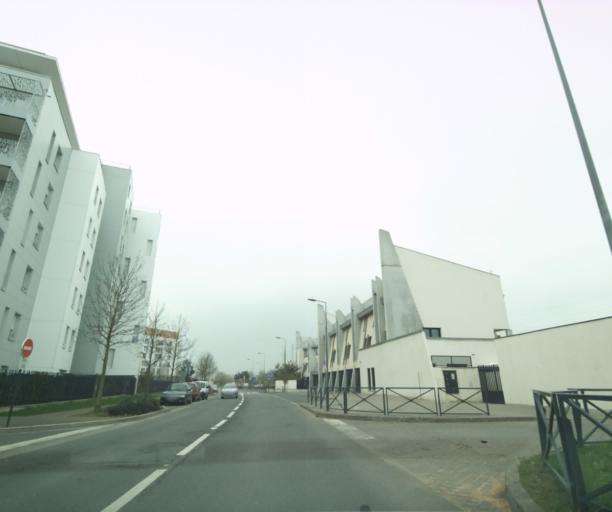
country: FR
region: Ile-de-France
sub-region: Departement du Val-d'Oise
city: Courdimanche
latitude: 49.0524
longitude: 2.0078
